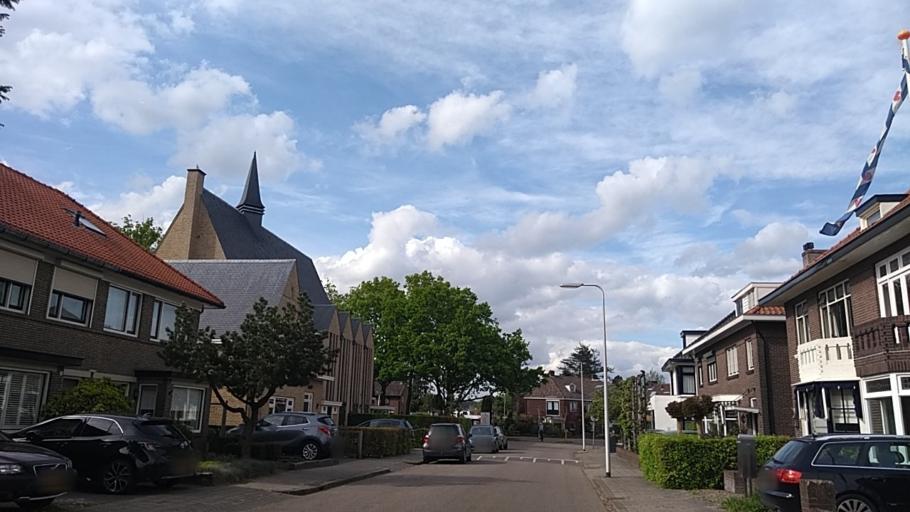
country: NL
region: Overijssel
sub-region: Gemeente Almelo
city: Almelo
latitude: 52.3630
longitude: 6.6624
